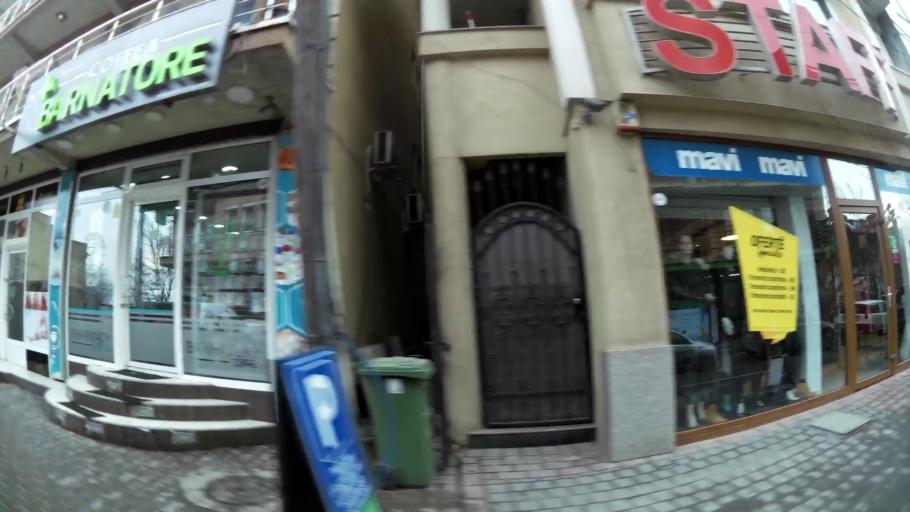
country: XK
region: Pristina
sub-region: Komuna e Prishtines
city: Pristina
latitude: 42.6670
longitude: 21.1751
